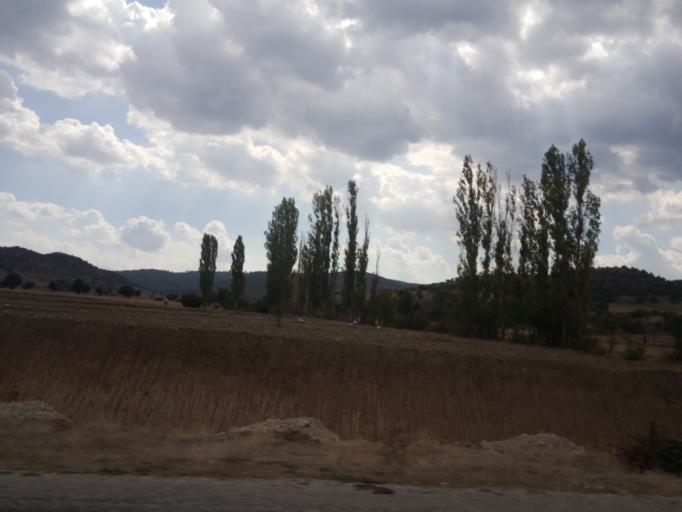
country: TR
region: Yozgat
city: Cekerek
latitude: 40.1929
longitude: 35.4276
